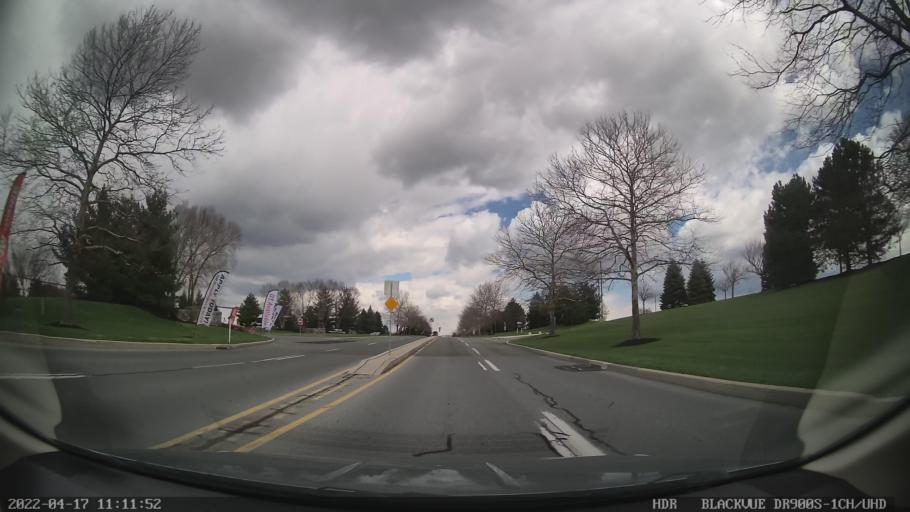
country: US
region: Pennsylvania
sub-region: Lehigh County
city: Breinigsville
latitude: 40.5533
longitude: -75.6242
